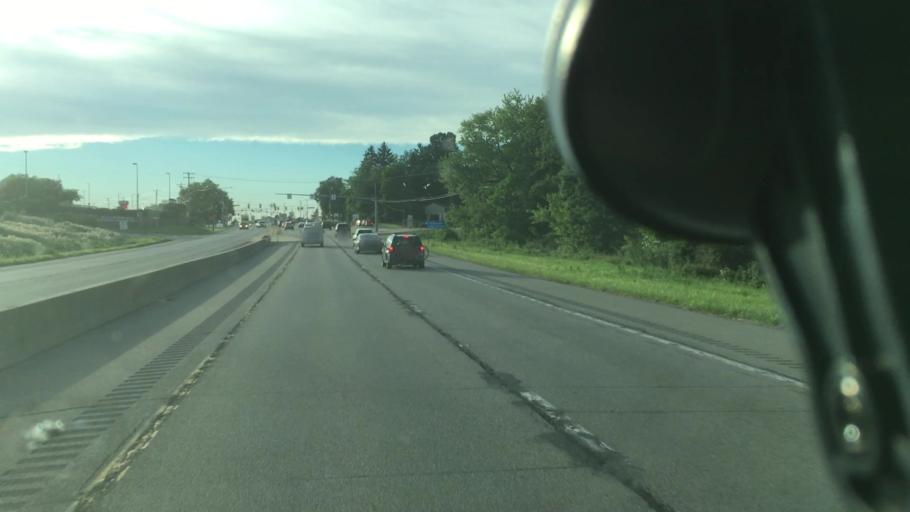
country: US
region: Pennsylvania
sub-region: Beaver County
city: West Mayfield
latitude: 40.7698
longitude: -80.3693
